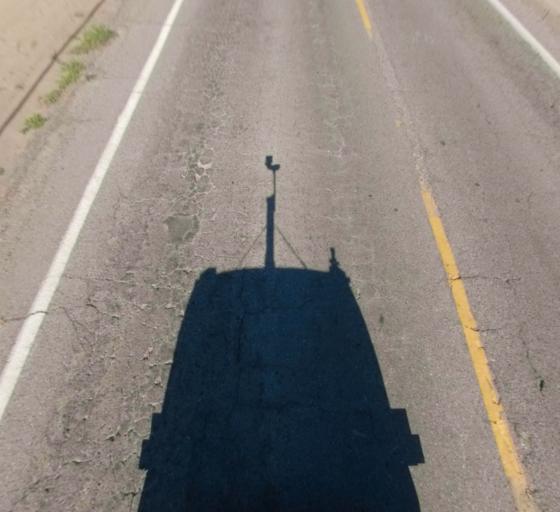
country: US
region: California
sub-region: Fresno County
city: Biola
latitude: 36.8513
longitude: -120.0495
